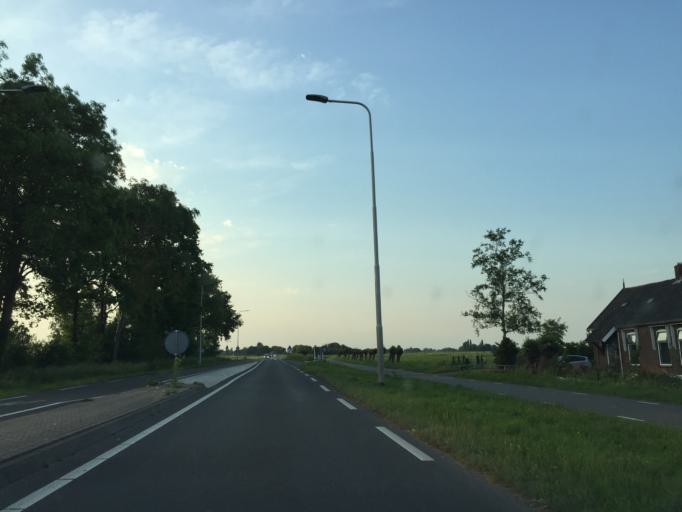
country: NL
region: South Holland
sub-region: Molenwaard
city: Liesveld
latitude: 51.9429
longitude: 4.7799
